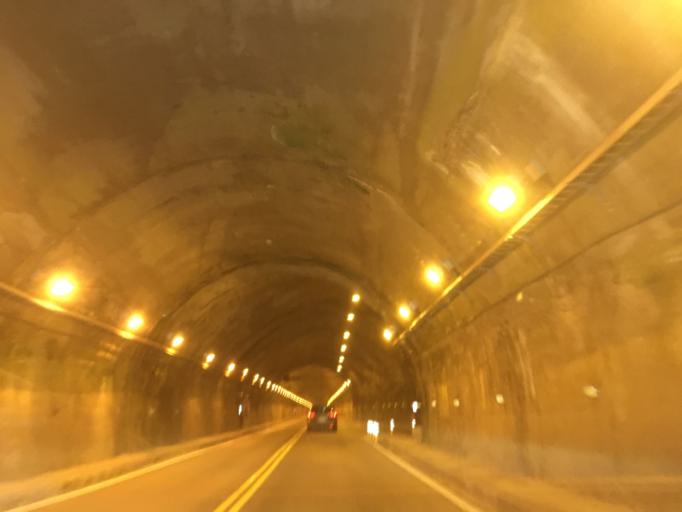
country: TW
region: Taiwan
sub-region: Hualien
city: Hualian
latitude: 24.1605
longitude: 121.6098
